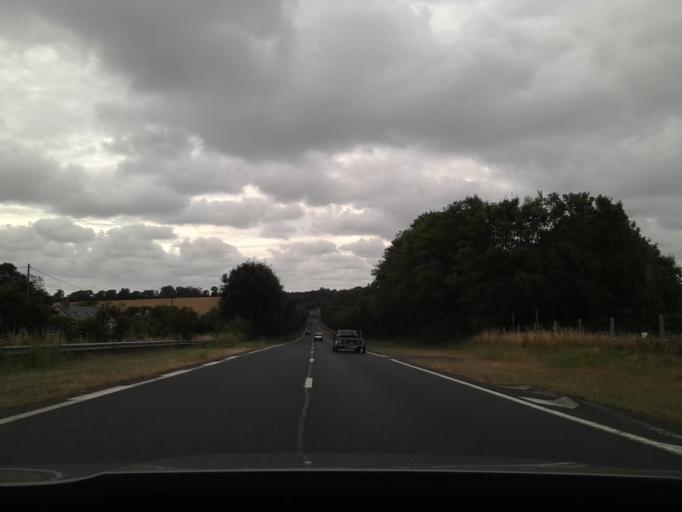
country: FR
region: Lower Normandy
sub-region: Departement du Calvados
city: Le Molay-Littry
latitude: 49.3215
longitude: -0.8621
